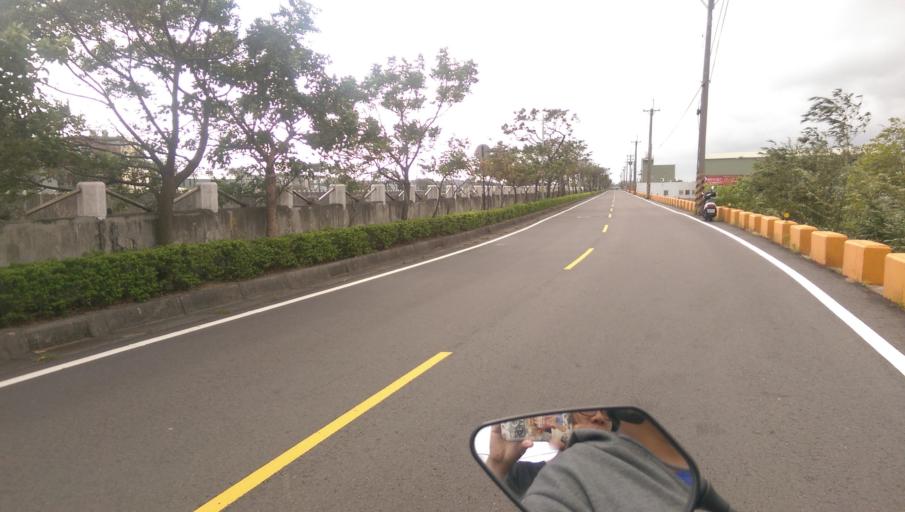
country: TW
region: Taiwan
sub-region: Hsinchu
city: Hsinchu
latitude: 24.8051
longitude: 120.9311
